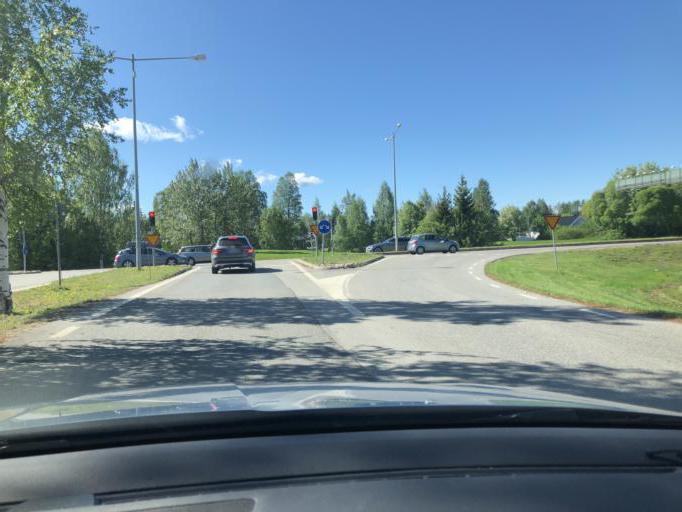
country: SE
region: Norrbotten
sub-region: Pitea Kommun
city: Pitea
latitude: 65.3121
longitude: 21.4915
